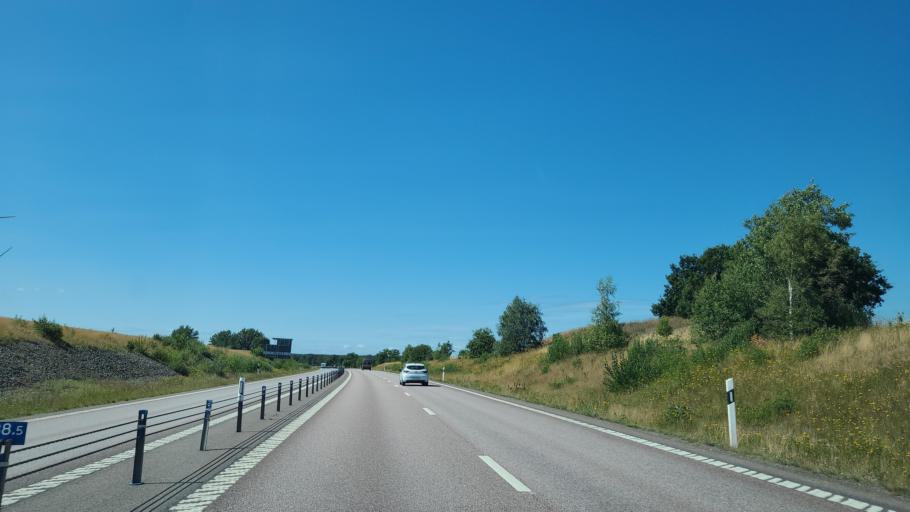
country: SE
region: Kalmar
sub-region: Kalmar Kommun
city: Ljungbyholm
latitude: 56.6167
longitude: 16.1562
